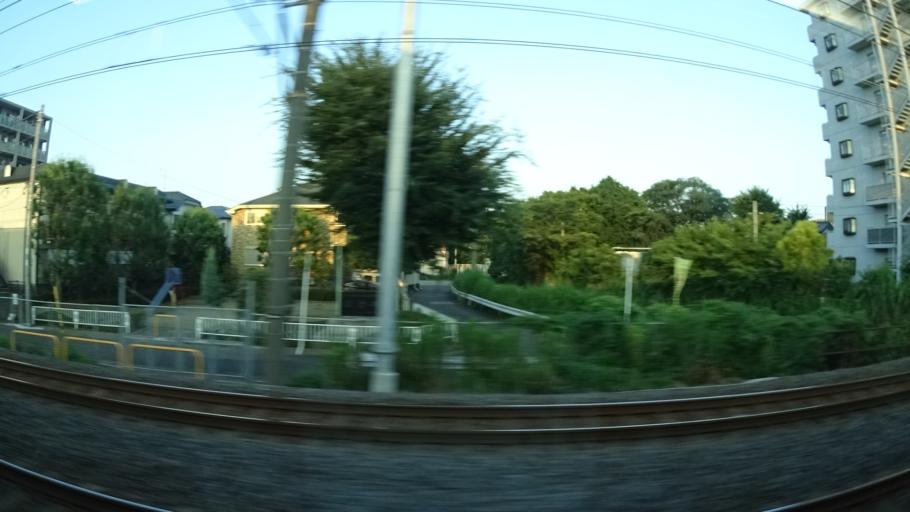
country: JP
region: Chiba
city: Nagareyama
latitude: 35.8217
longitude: 139.9198
